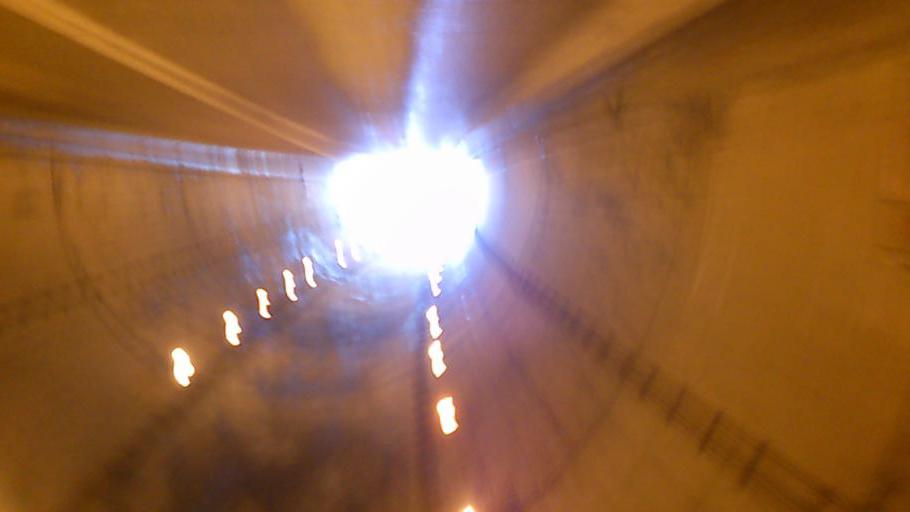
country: JP
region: Aomori
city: Hirosaki
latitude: 40.5344
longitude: 140.2567
